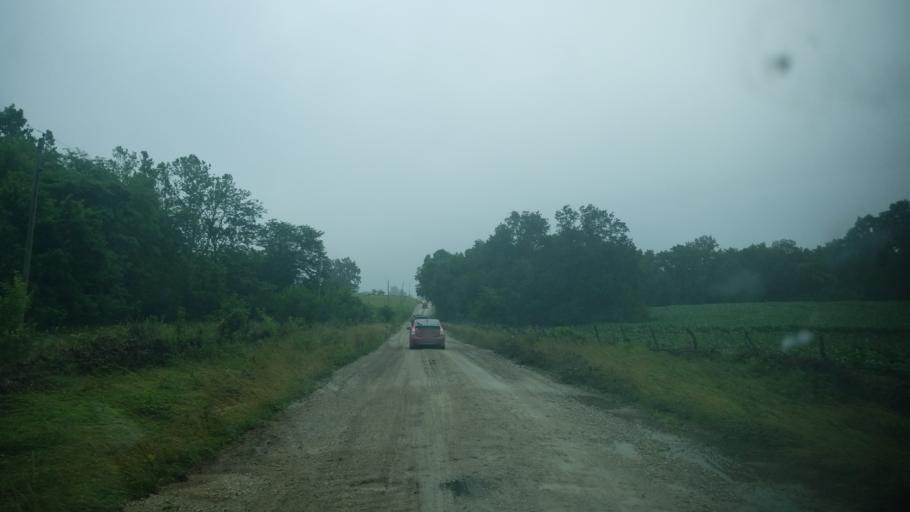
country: US
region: Missouri
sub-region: Pike County
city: Bowling Green
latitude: 39.3066
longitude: -91.2890
